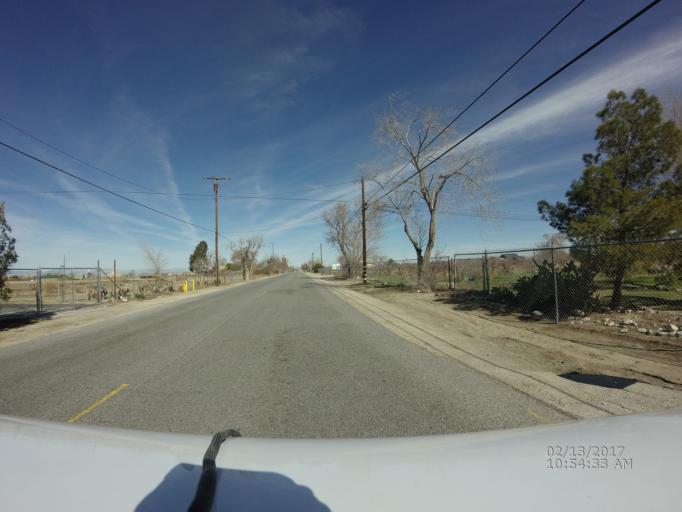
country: US
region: California
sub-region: Los Angeles County
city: Littlerock
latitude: 34.5374
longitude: -117.9837
